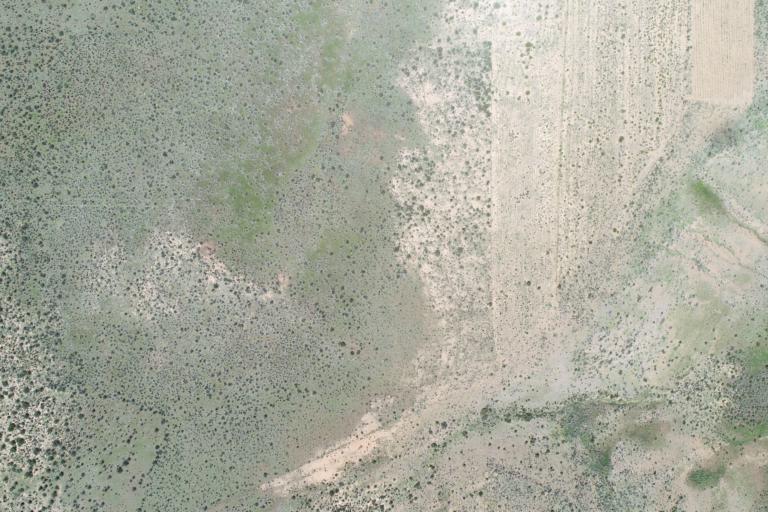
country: BO
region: La Paz
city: Curahuara de Carangas
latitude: -17.3204
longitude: -68.5028
